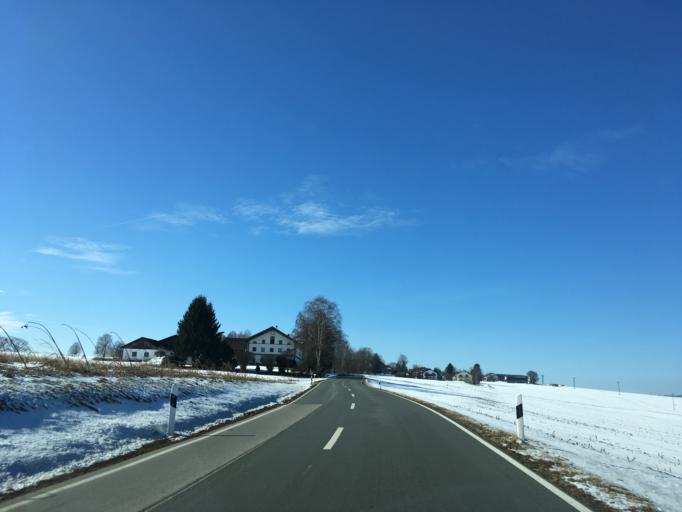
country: DE
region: Bavaria
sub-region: Upper Bavaria
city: Albaching
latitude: 48.1134
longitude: 12.1358
